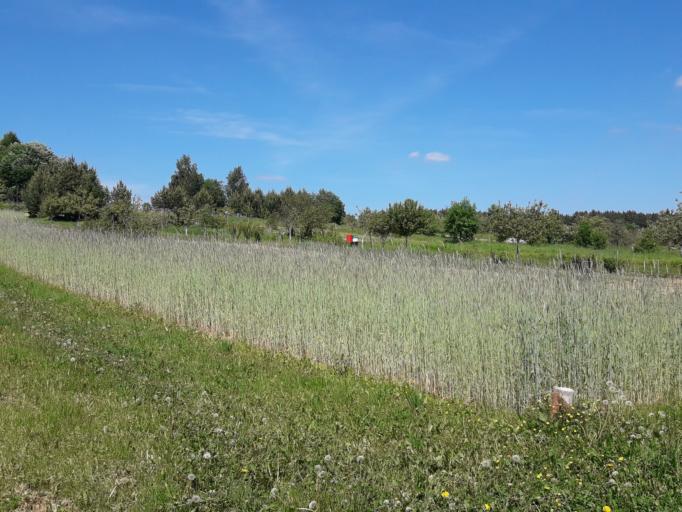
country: BY
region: Minsk
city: Pyatryshki
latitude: 54.1292
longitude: 27.1330
